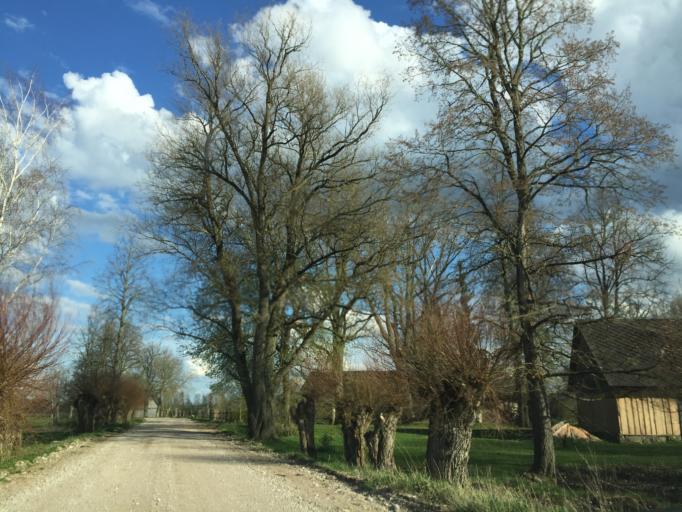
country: LV
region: Beverina
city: Murmuiza
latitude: 57.3713
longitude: 25.4967
